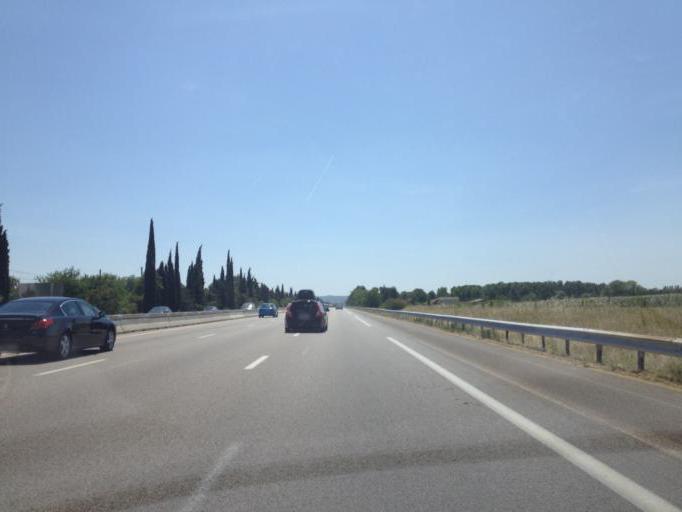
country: FR
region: Rhone-Alpes
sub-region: Departement de la Drome
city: Etoile-sur-Rhone
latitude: 44.8441
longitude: 4.8643
